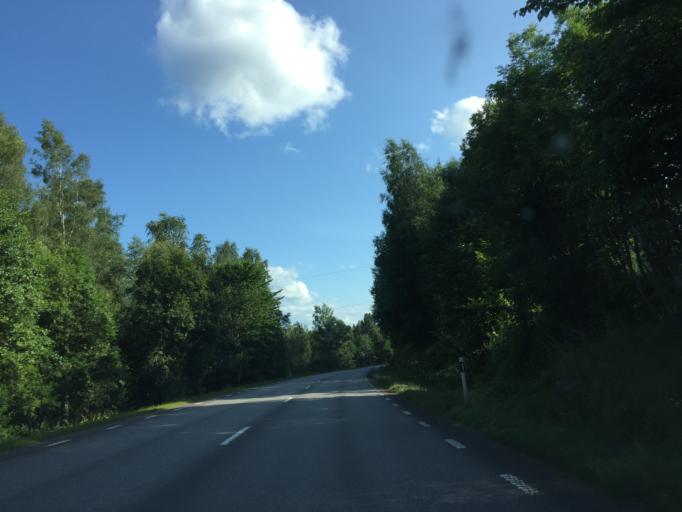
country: SE
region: OErebro
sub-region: Askersunds Kommun
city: Asbro
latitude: 58.9286
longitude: 15.0001
